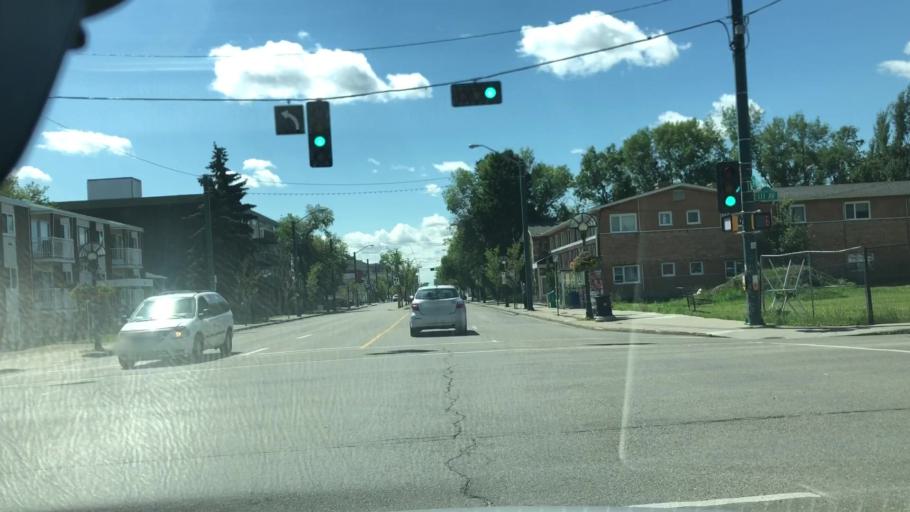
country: CA
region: Alberta
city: Edmonton
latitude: 53.5589
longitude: -113.5360
